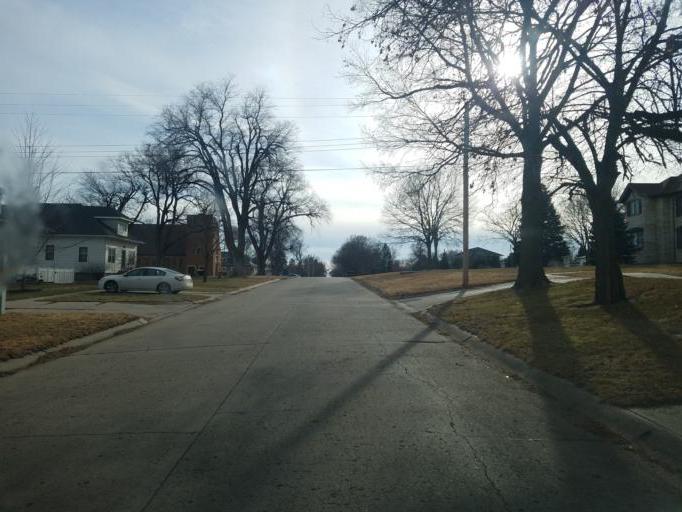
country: US
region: Nebraska
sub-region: Knox County
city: Creighton
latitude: 42.4641
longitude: -97.9063
